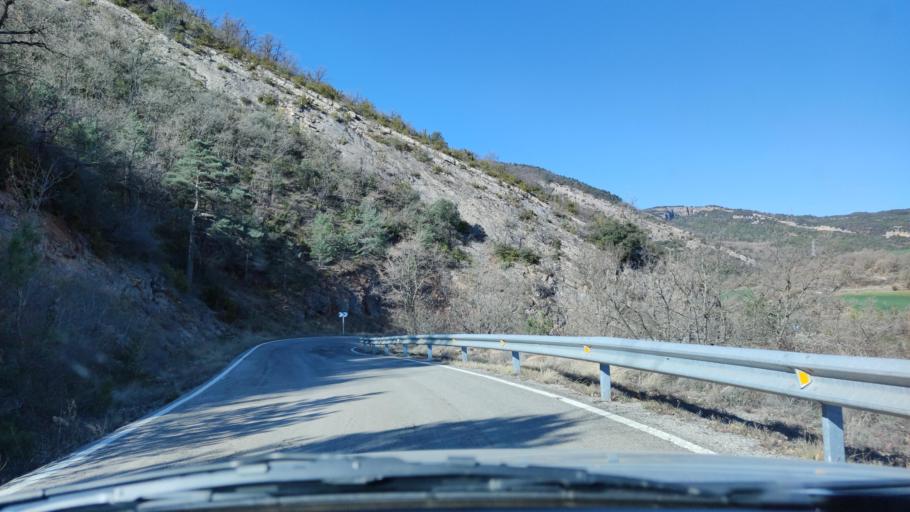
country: ES
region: Catalonia
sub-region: Provincia de Lleida
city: Llimiana
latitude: 42.0449
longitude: 1.0417
